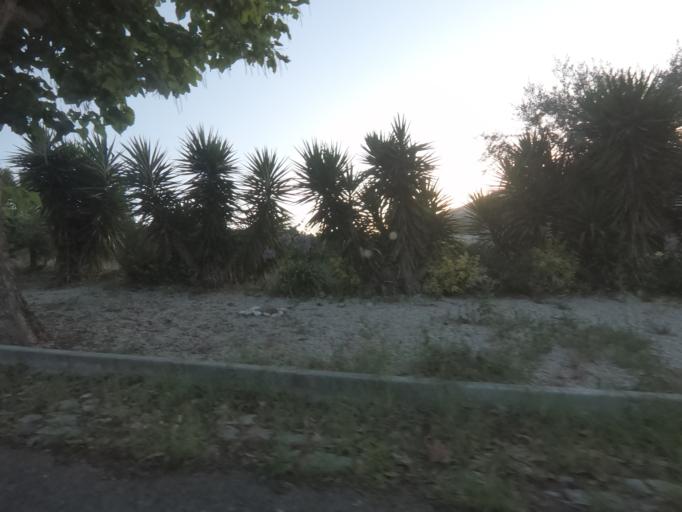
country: PT
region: Vila Real
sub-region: Peso da Regua
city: Peso da Regua
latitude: 41.1642
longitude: -7.7601
